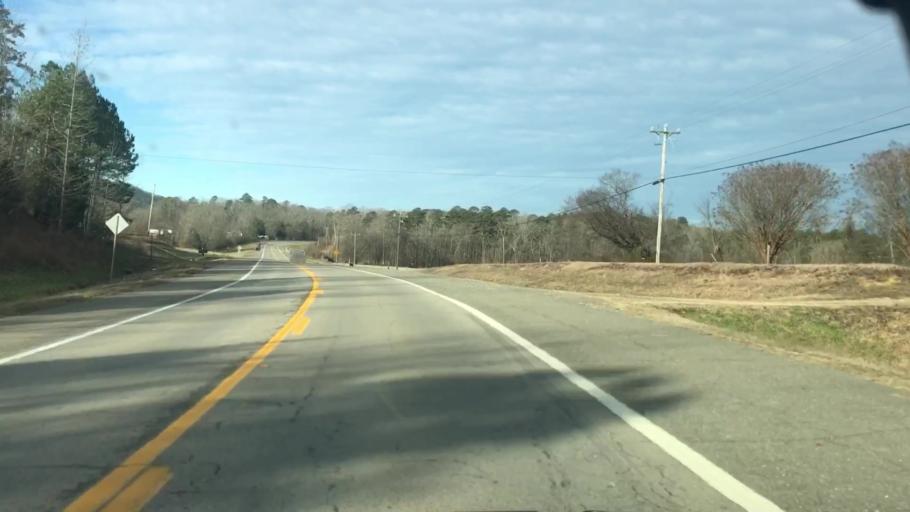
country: US
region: Arkansas
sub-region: Montgomery County
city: Mount Ida
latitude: 34.5401
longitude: -93.5967
